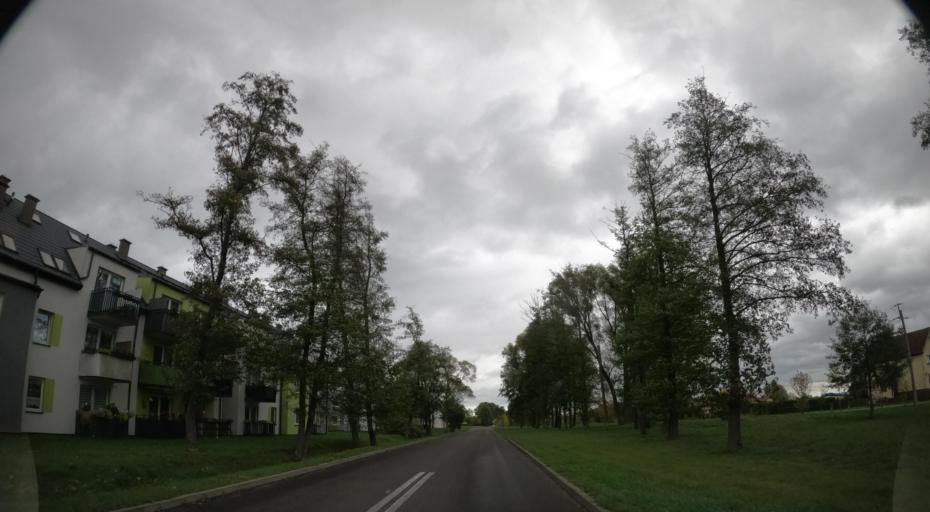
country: PL
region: West Pomeranian Voivodeship
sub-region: Powiat goleniowski
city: Stepnica
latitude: 53.6498
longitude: 14.6275
